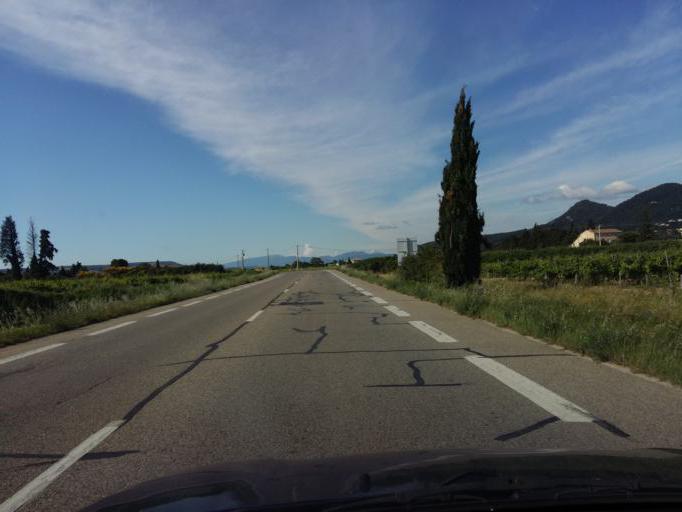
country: FR
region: Provence-Alpes-Cote d'Azur
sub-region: Departement du Vaucluse
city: Sablet
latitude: 44.1965
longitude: 4.9985
